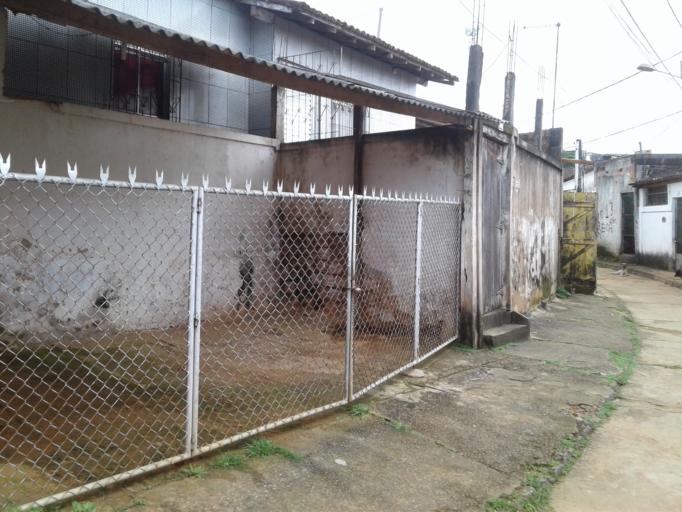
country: BR
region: Bahia
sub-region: Salvador
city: Salvador
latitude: -12.9099
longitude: -38.4728
